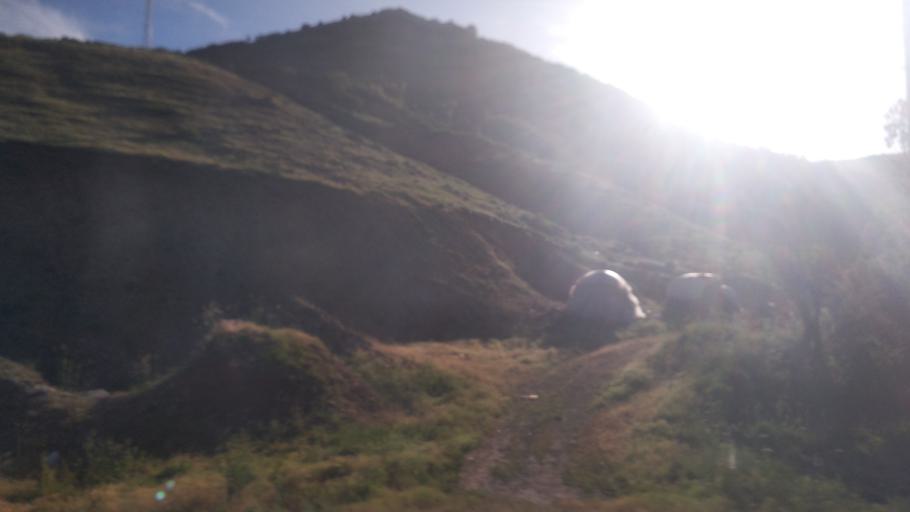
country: TR
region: Bitlis
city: Resadiye
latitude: 38.4556
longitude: 42.5414
